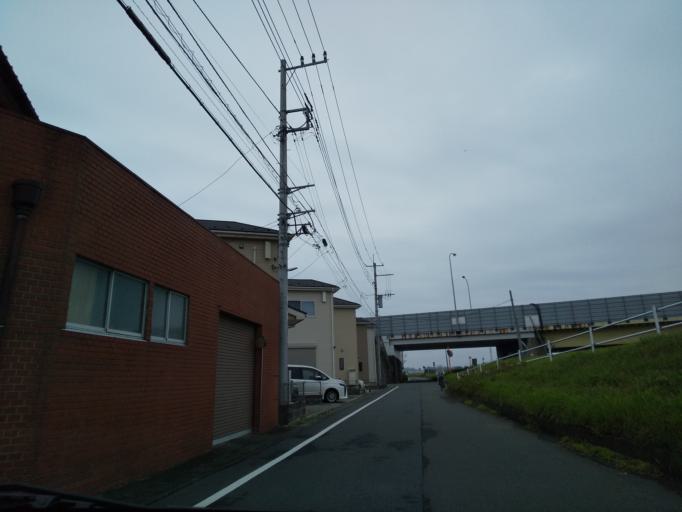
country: JP
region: Tokyo
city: Hino
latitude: 35.6766
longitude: 139.4208
